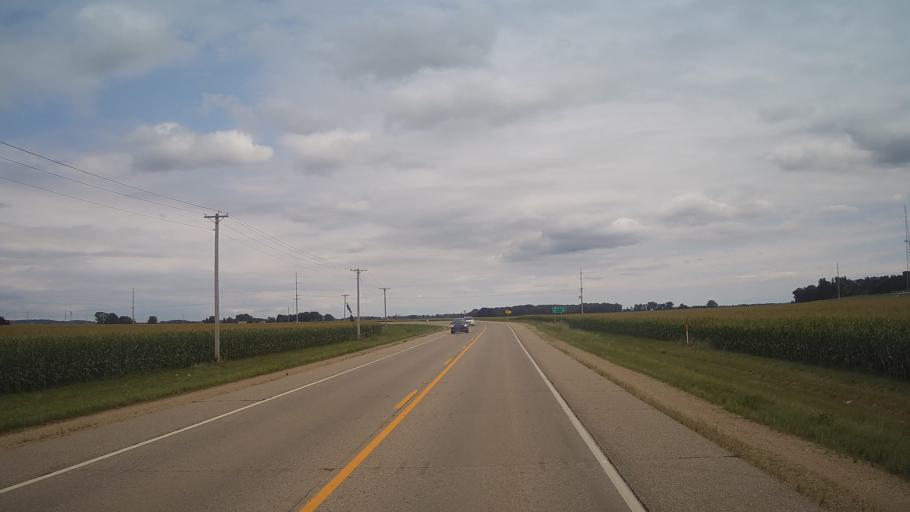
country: US
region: Wisconsin
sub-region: Waushara County
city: Redgranite
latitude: 44.0376
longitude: -89.0503
